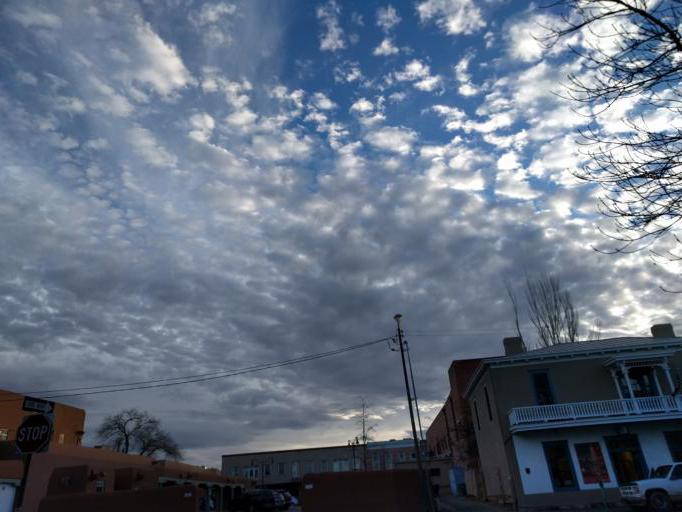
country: US
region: New Mexico
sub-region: Santa Fe County
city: Santa Fe
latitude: 35.6883
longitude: -105.9397
